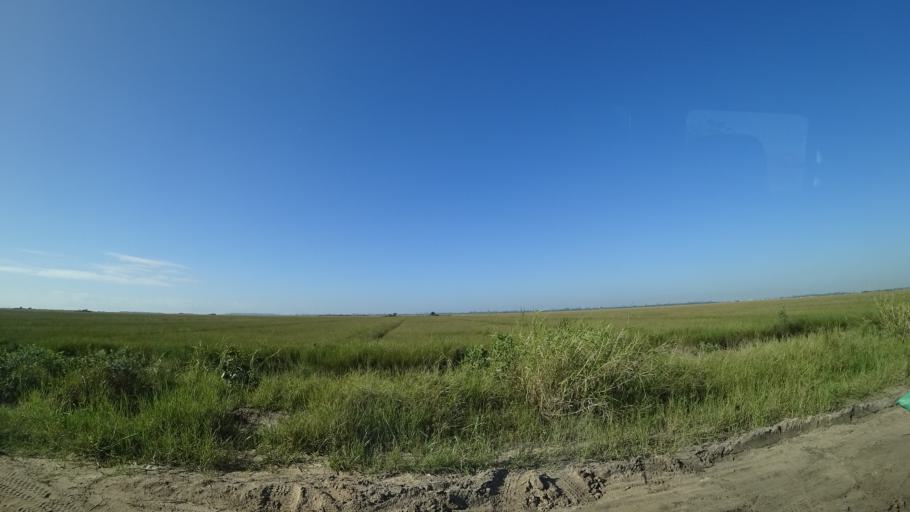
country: MZ
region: Sofala
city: Beira
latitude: -19.7569
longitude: 34.9218
